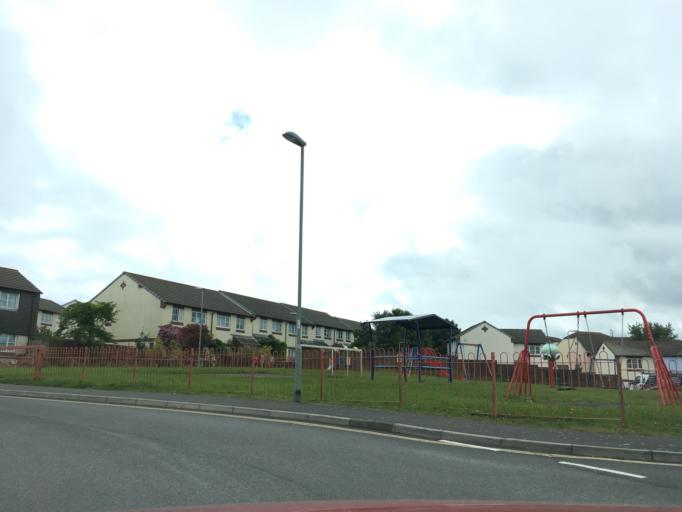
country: GB
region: England
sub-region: Devon
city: Dartmouth
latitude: 50.3493
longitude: -3.6010
